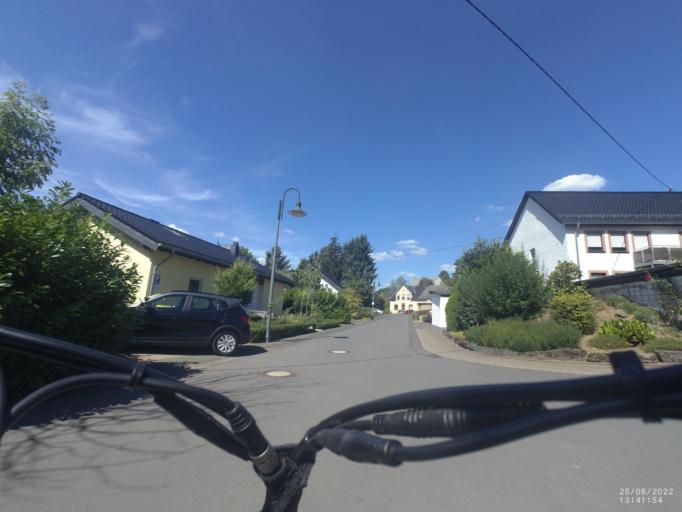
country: DE
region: Rheinland-Pfalz
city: Hohenfels-Essingen
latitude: 50.2494
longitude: 6.7320
